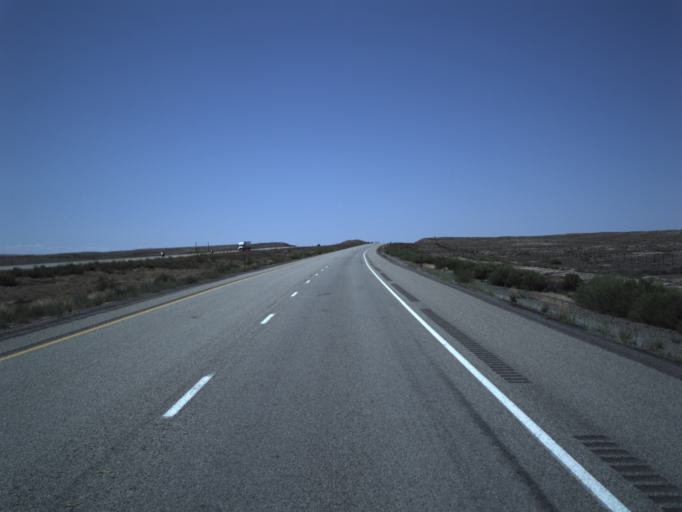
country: US
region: Utah
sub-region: Grand County
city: Moab
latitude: 39.0121
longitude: -109.3068
